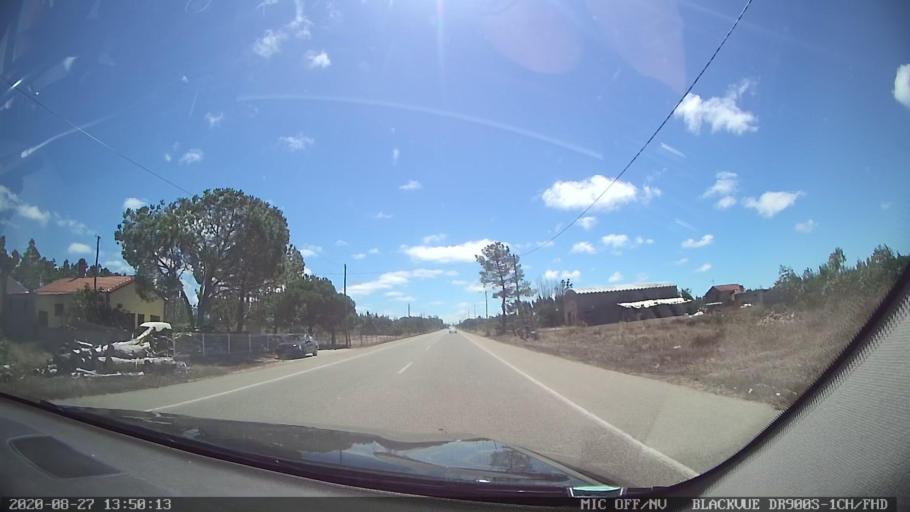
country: PT
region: Coimbra
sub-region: Mira
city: Mira
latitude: 40.3591
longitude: -8.7474
